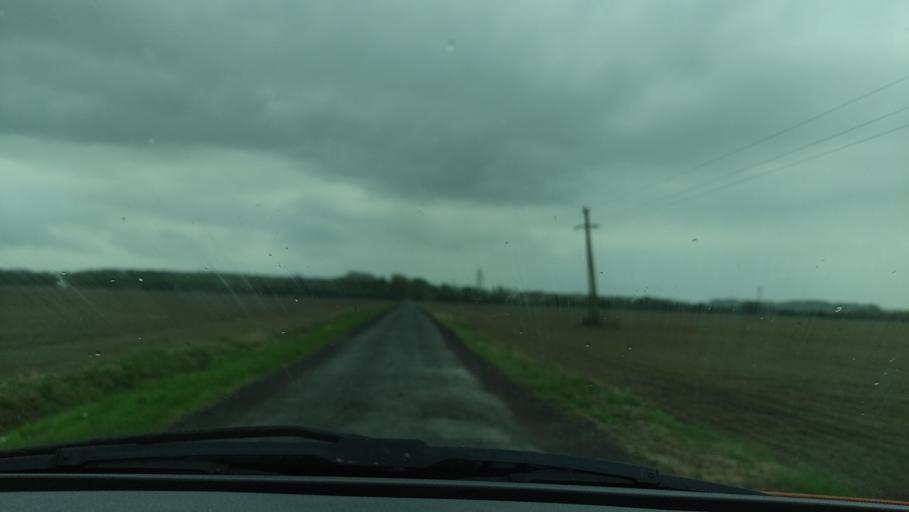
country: HR
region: Osjecko-Baranjska
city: Batina
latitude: 45.9034
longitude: 18.7706
